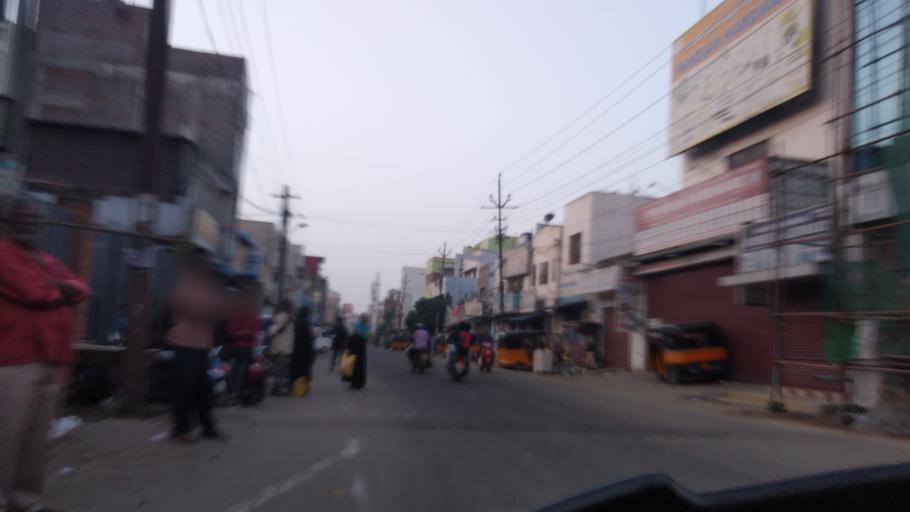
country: IN
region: Tamil Nadu
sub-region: Coimbatore
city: Coimbatore
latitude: 11.0005
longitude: 76.9598
